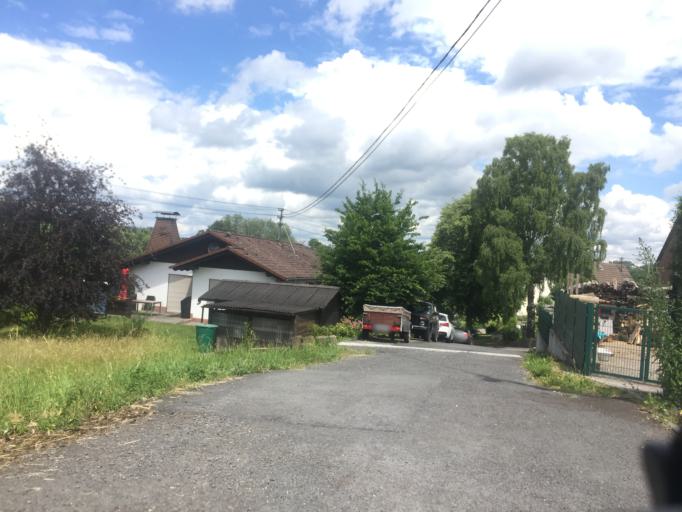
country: DE
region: Rheinland-Pfalz
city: Steinefrenz
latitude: 50.4575
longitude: 7.9282
